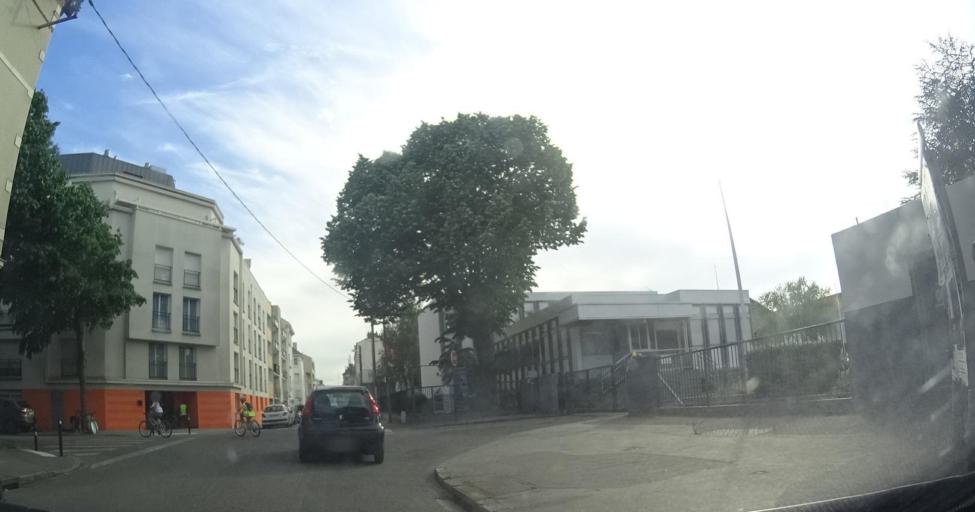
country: FR
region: Pays de la Loire
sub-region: Departement de la Loire-Atlantique
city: Nantes
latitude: 47.2235
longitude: -1.5330
